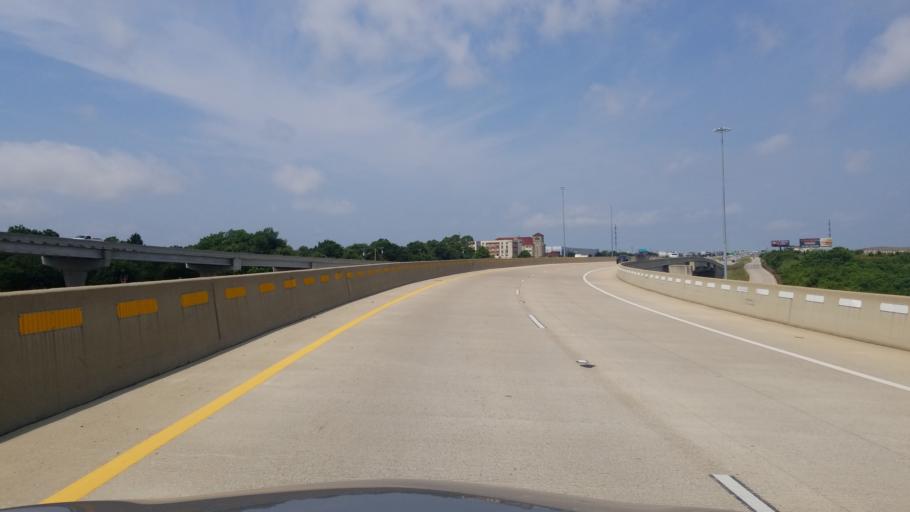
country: US
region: Texas
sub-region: Dallas County
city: Grand Prairie
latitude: 32.6767
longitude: -97.0260
